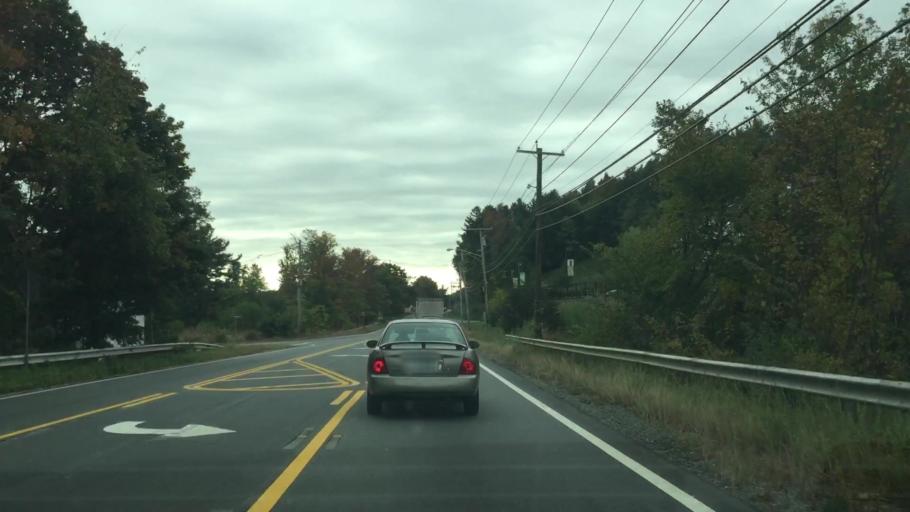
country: US
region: Massachusetts
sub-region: Essex County
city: Andover
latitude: 42.6509
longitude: -71.0950
